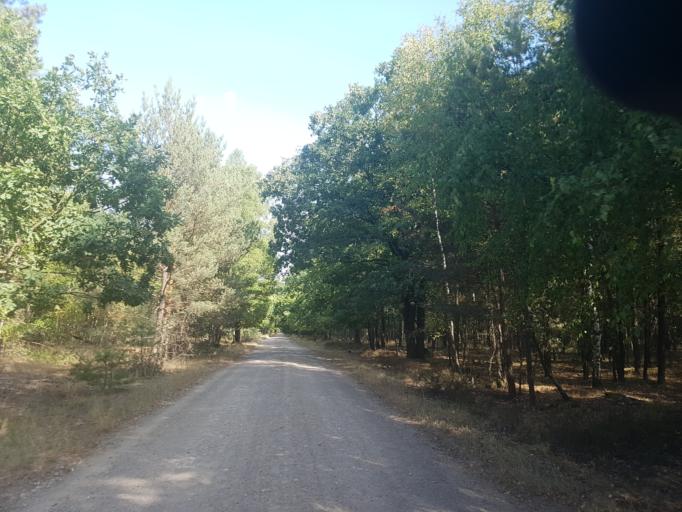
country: DE
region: Saxony-Anhalt
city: Jessen
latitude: 51.8703
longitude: 13.0001
